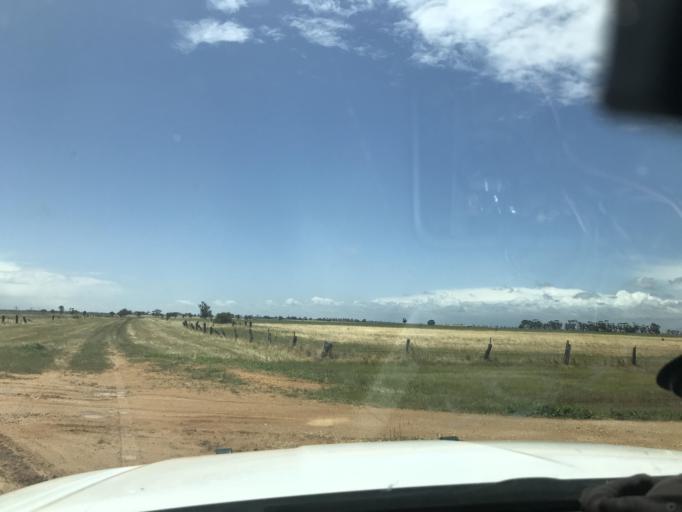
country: AU
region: South Australia
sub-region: Tatiara
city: Bordertown
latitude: -36.3758
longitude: 140.9913
